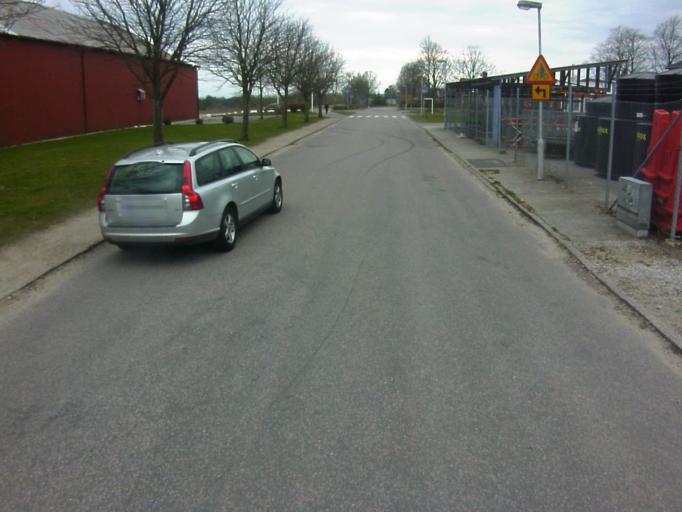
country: SE
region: Skane
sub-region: Kavlinge Kommun
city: Kaevlinge
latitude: 55.7891
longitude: 13.1004
